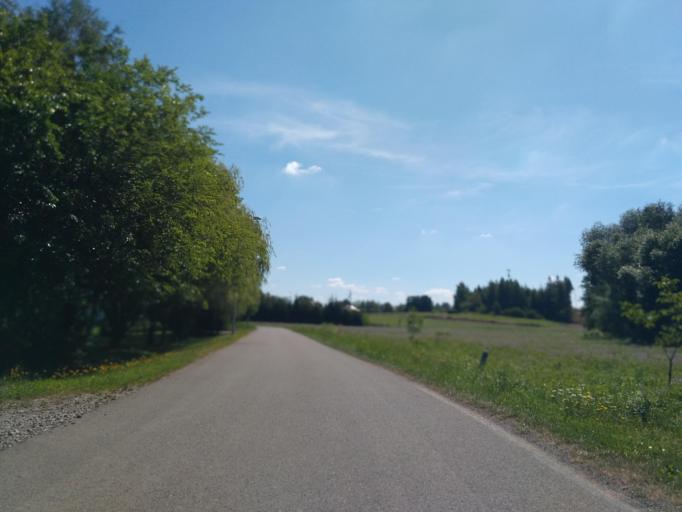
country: PL
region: Subcarpathian Voivodeship
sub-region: Powiat sanocki
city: Dlugie
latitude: 49.5700
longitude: 22.0486
